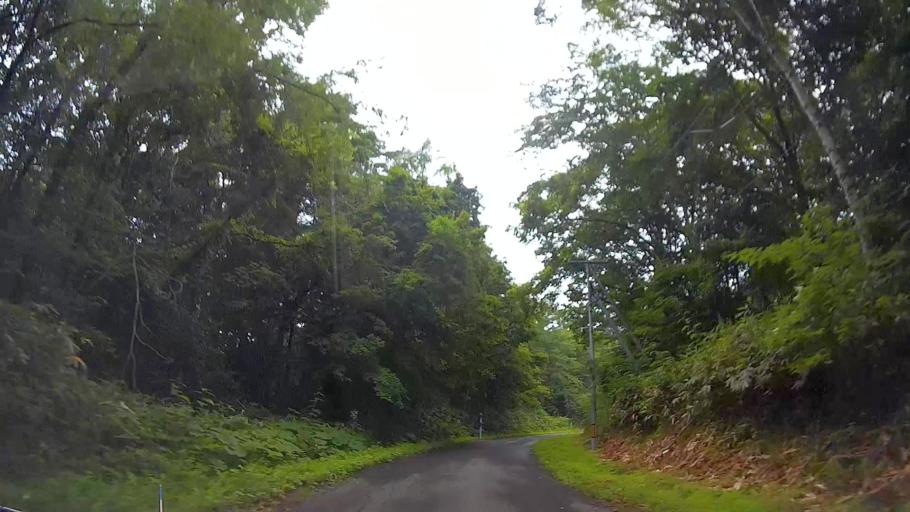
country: JP
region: Hokkaido
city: Nanae
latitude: 42.0671
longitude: 140.5062
